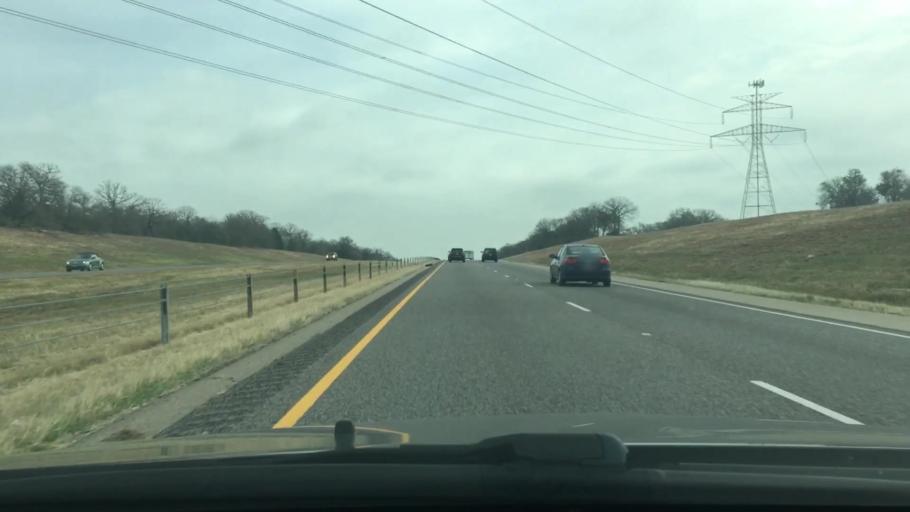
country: US
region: Texas
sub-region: Leon County
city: Buffalo
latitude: 31.5339
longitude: -96.1187
